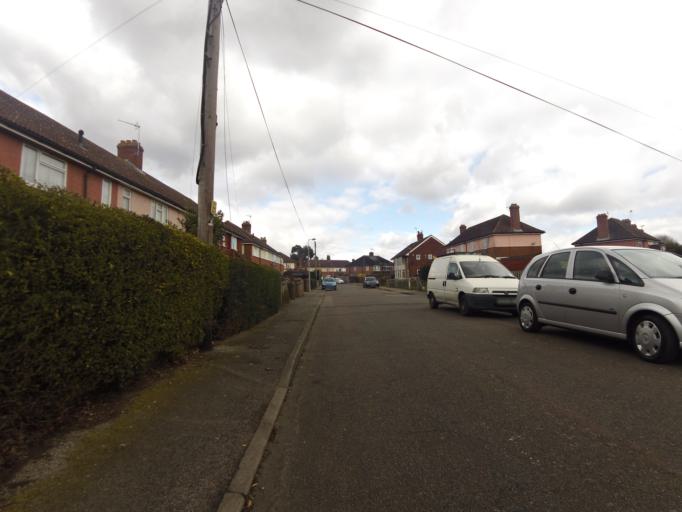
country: GB
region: England
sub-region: Suffolk
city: Ipswich
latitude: 52.0304
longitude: 1.1794
